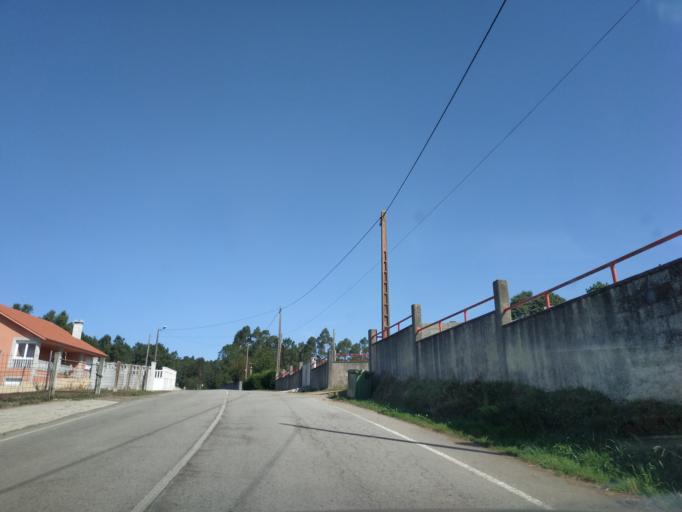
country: ES
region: Galicia
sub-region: Provincia da Coruna
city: Laracha
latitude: 43.2260
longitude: -8.5416
